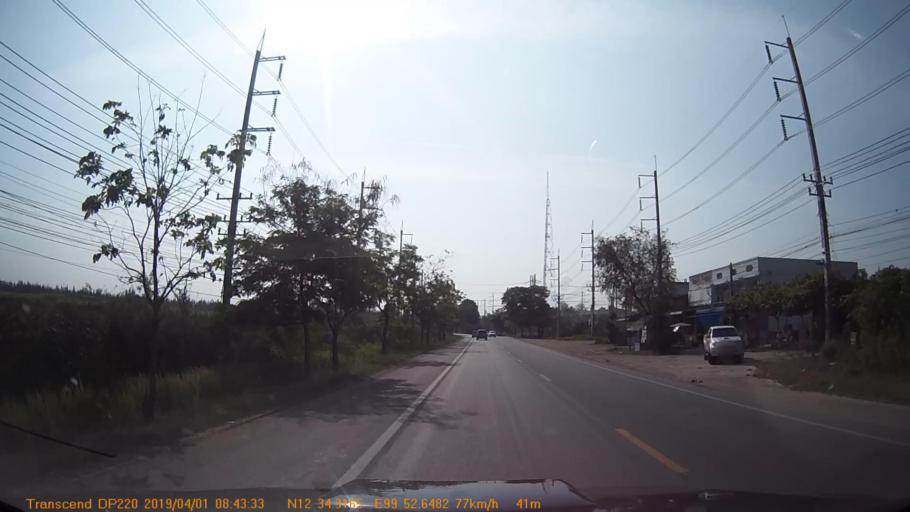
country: TH
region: Prachuap Khiri Khan
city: Hua Hin
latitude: 12.5718
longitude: 99.8779
